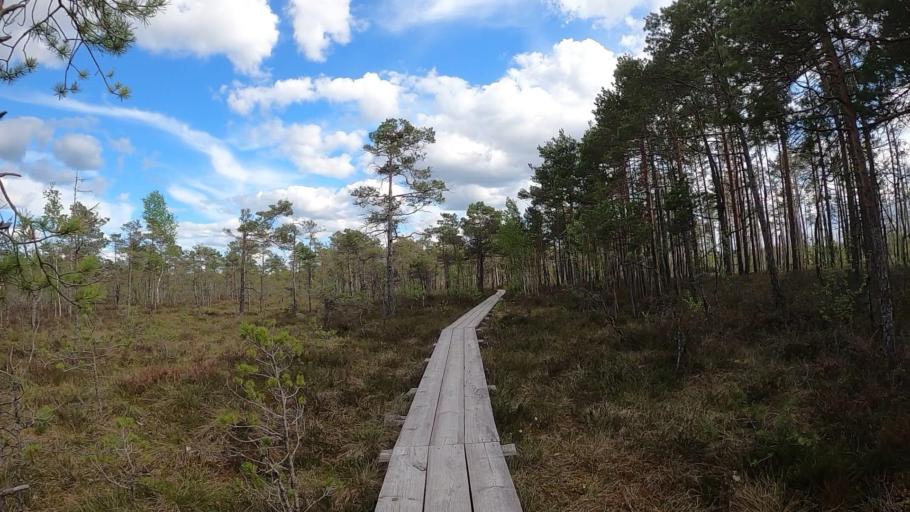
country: LV
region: Jurmala
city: Jurmala
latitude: 56.8531
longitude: 23.8134
